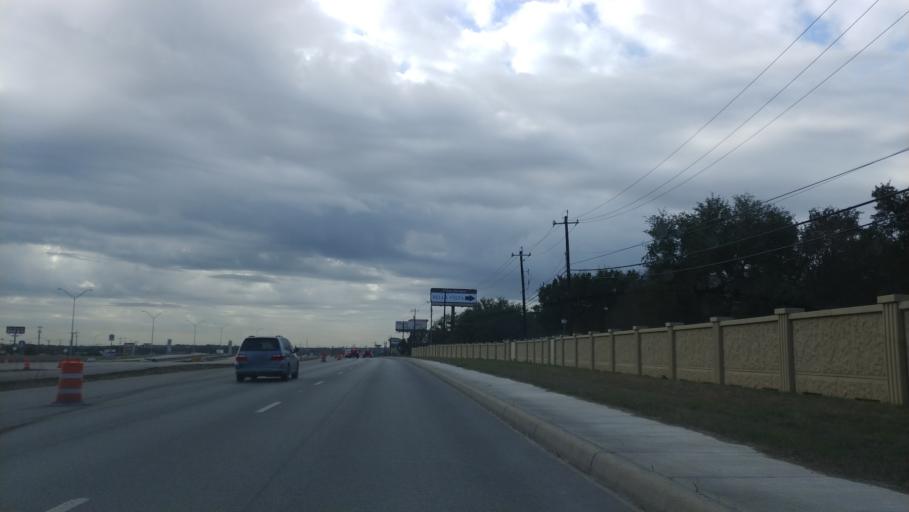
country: US
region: Texas
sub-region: Bexar County
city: Lackland Air Force Base
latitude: 29.4403
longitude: -98.7120
